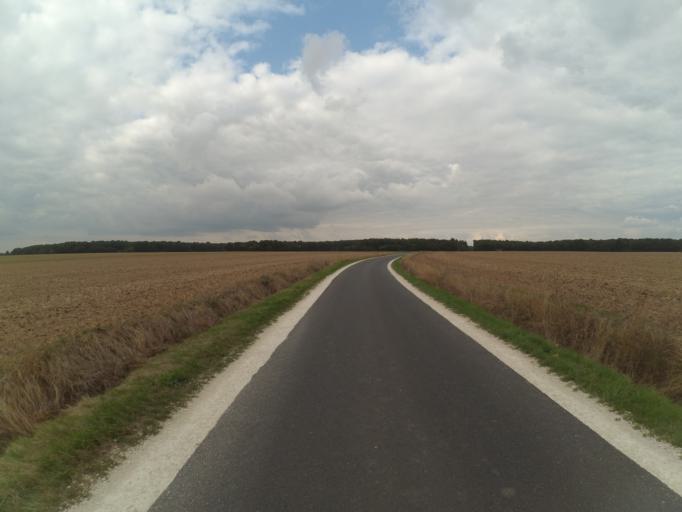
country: FR
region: Centre
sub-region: Departement d'Indre-et-Loire
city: Poce-sur-Cisse
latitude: 47.5039
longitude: 0.9728
